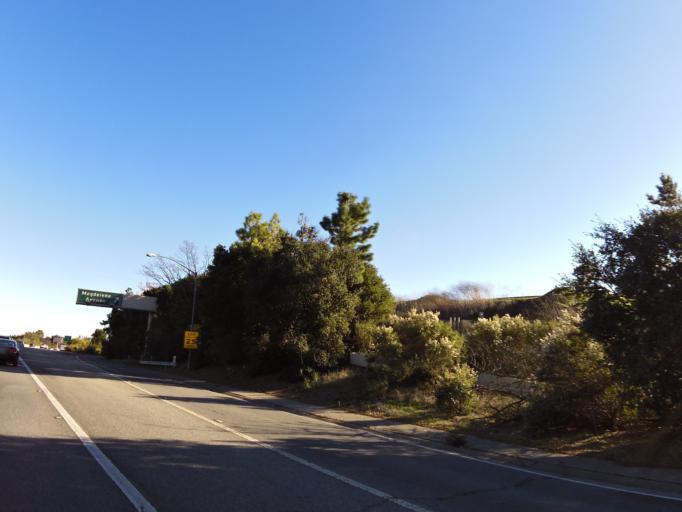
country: US
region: California
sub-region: Santa Clara County
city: Loyola
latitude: 37.3546
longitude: -122.1116
